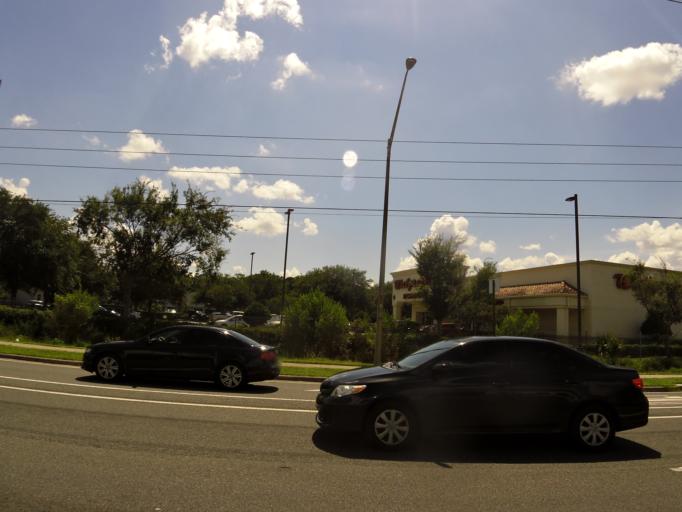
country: US
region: Florida
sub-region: Saint Johns County
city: Fruit Cove
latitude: 30.1662
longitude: -81.6016
